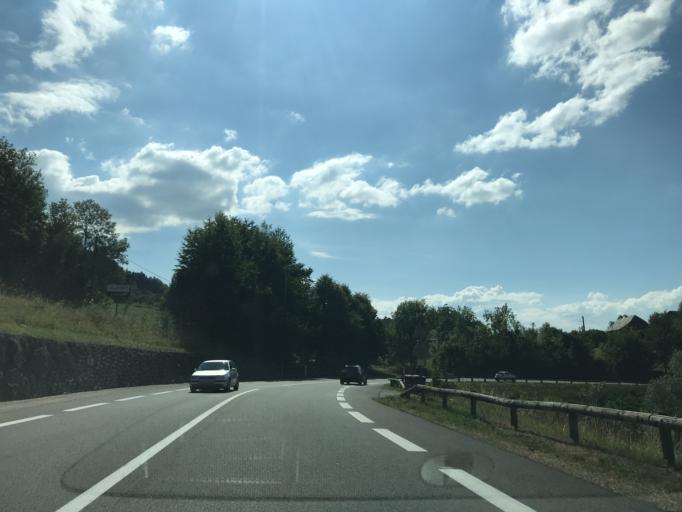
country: FR
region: Rhone-Alpes
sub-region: Departement de la Haute-Savoie
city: Villaz
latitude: 45.9202
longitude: 6.1826
